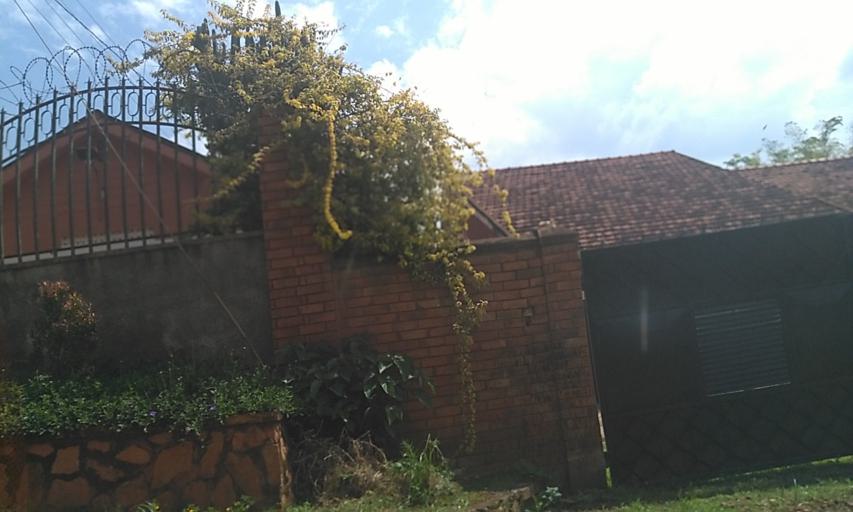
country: UG
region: Central Region
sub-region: Wakiso District
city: Kireka
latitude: 0.3499
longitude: 32.6118
